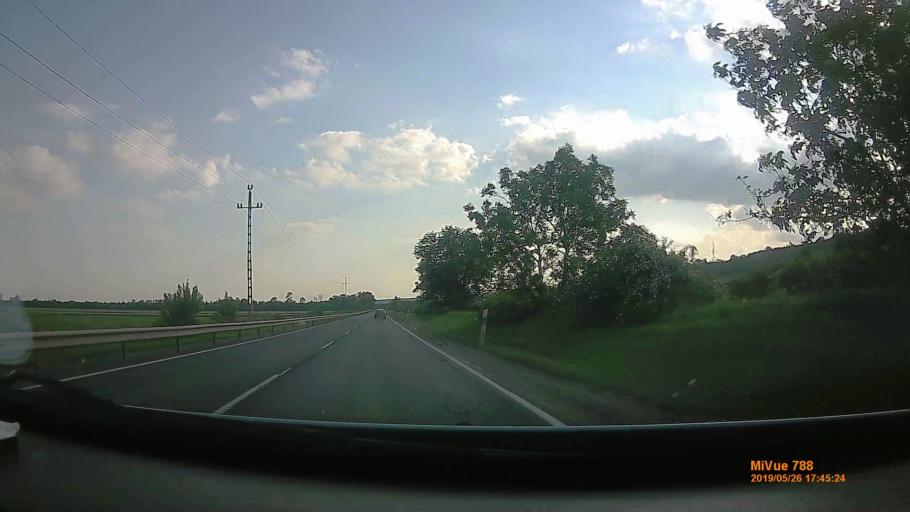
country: HU
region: Borsod-Abauj-Zemplen
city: Aszalo
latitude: 48.2175
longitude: 20.9501
